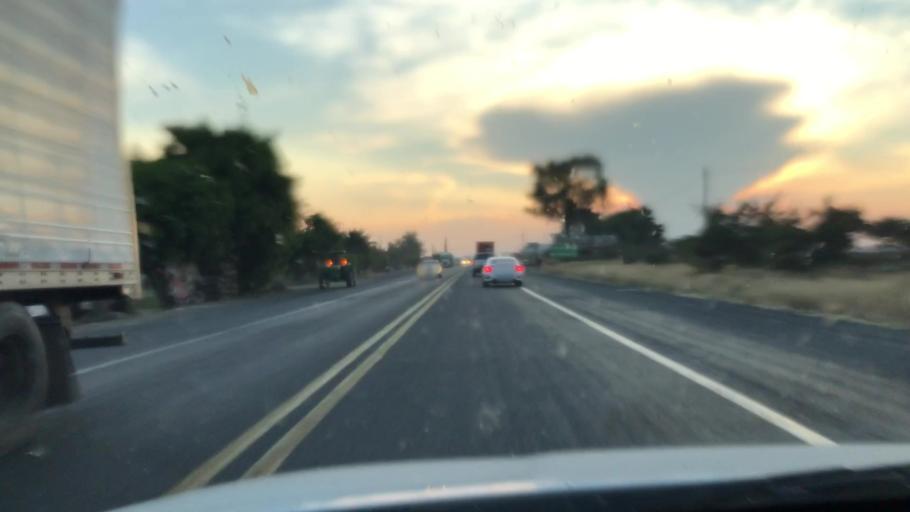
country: MX
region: Michoacan
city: Tanhuato de Guerrero
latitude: 20.3014
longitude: -102.3227
